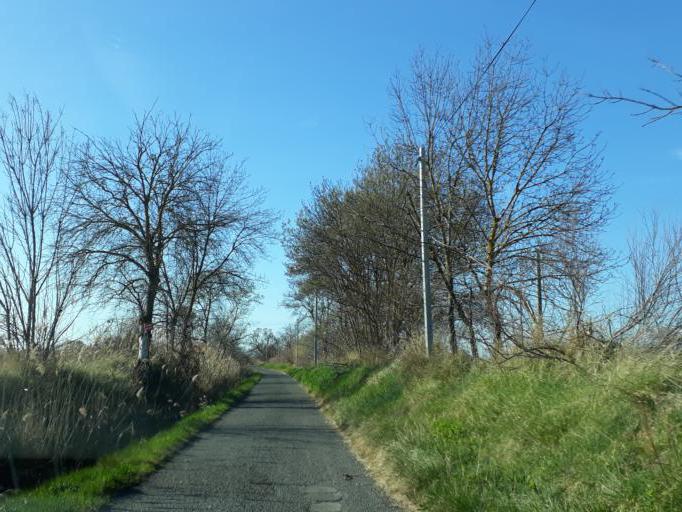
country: FR
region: Languedoc-Roussillon
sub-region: Departement de l'Herault
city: Agde
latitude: 43.3240
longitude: 3.4569
